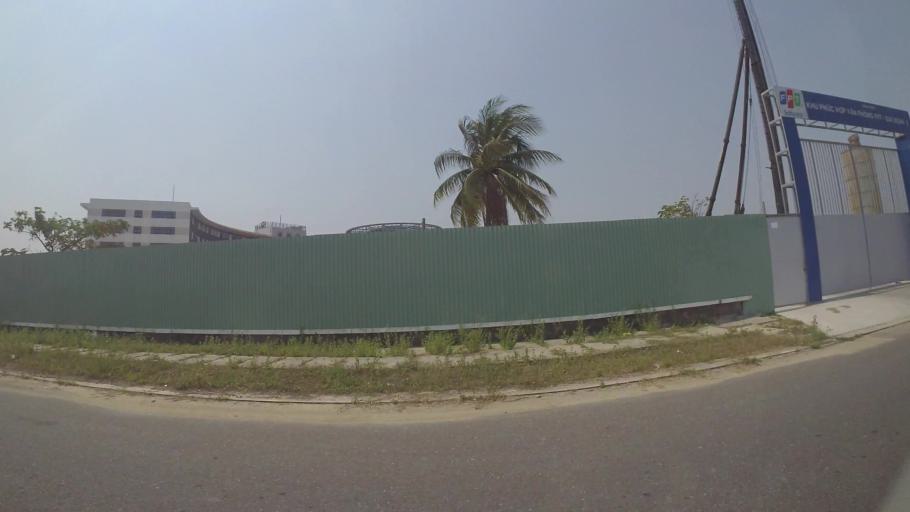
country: VN
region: Da Nang
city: Ngu Hanh Son
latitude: 15.9801
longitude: 108.2629
